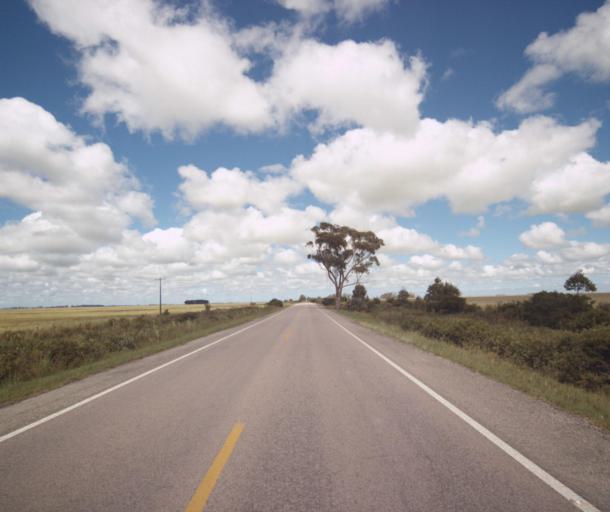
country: BR
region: Rio Grande do Sul
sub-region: Rio Grande
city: Rio Grande
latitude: -32.1724
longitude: -52.4144
